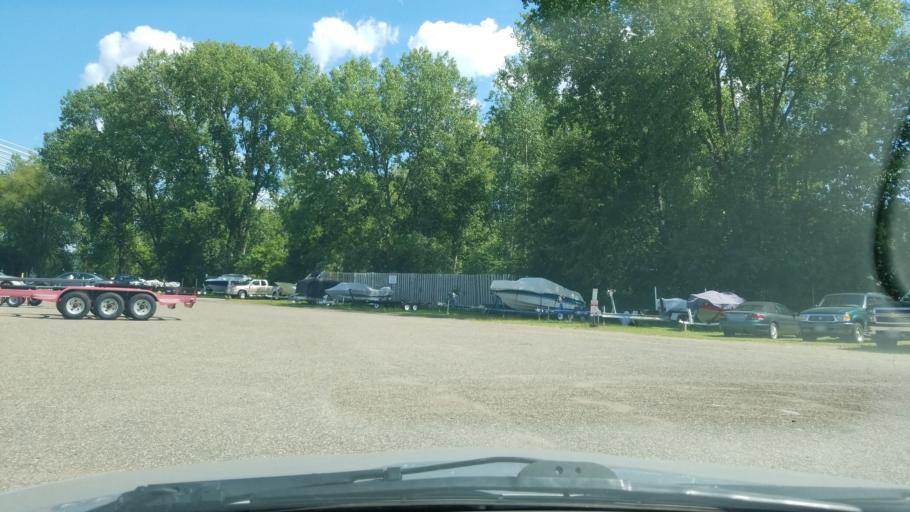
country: US
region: Minnesota
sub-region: Washington County
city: Oak Park Heights
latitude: 45.0396
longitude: -92.7909
